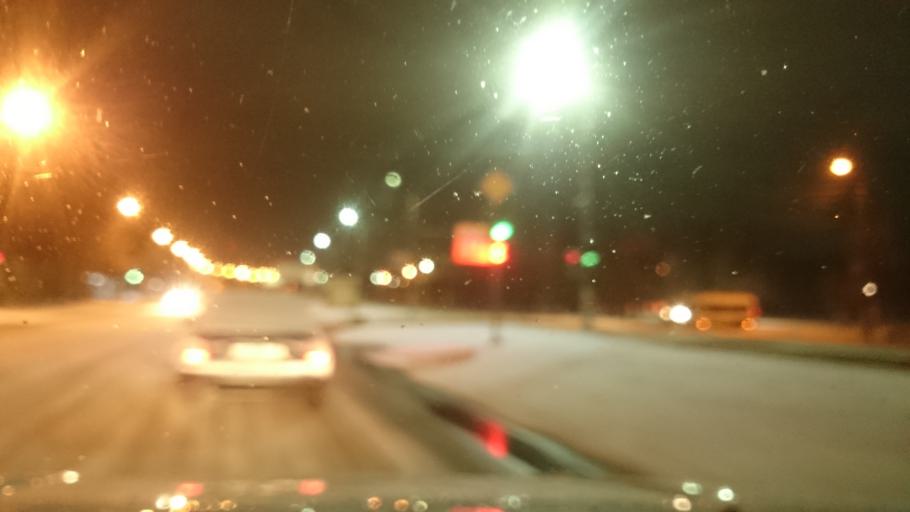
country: RU
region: Tula
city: Mendeleyevskiy
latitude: 54.1911
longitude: 37.5392
